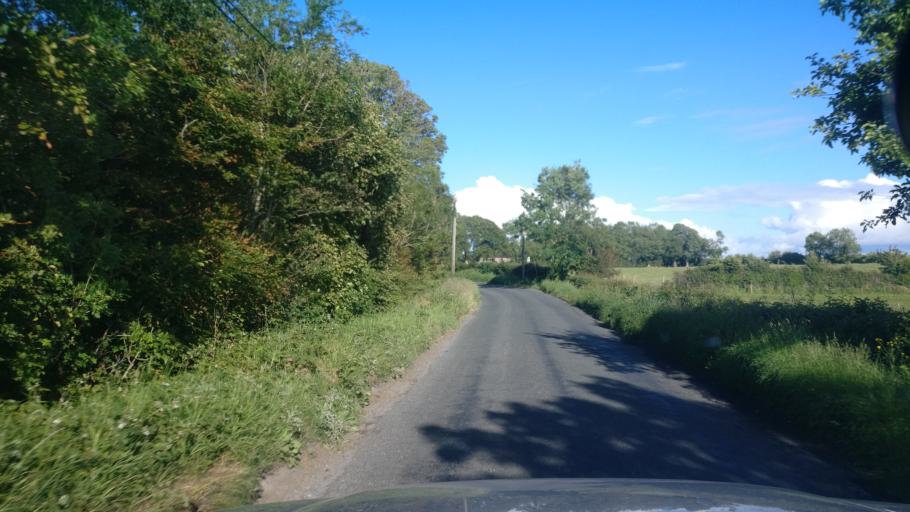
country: IE
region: Connaught
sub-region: County Galway
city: Ballinasloe
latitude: 53.2280
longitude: -8.2387
